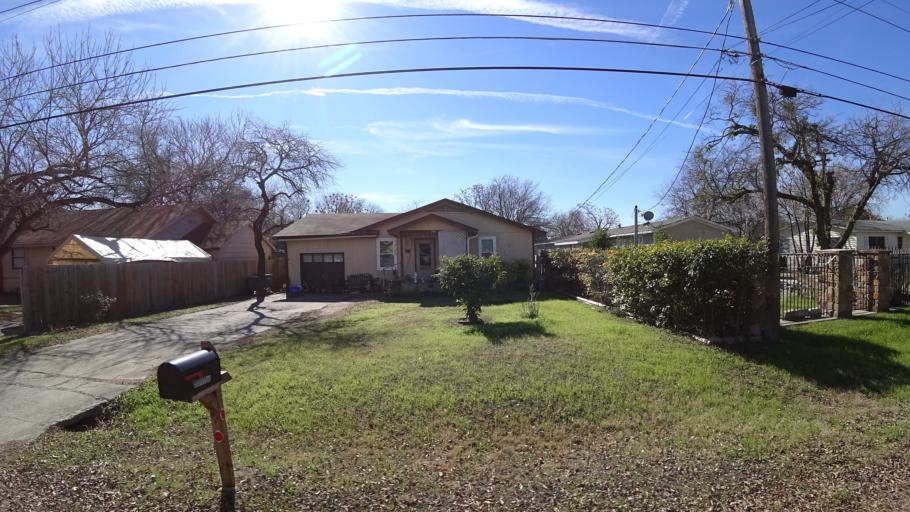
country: US
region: Texas
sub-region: Travis County
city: Wells Branch
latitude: 30.3756
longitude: -97.6867
